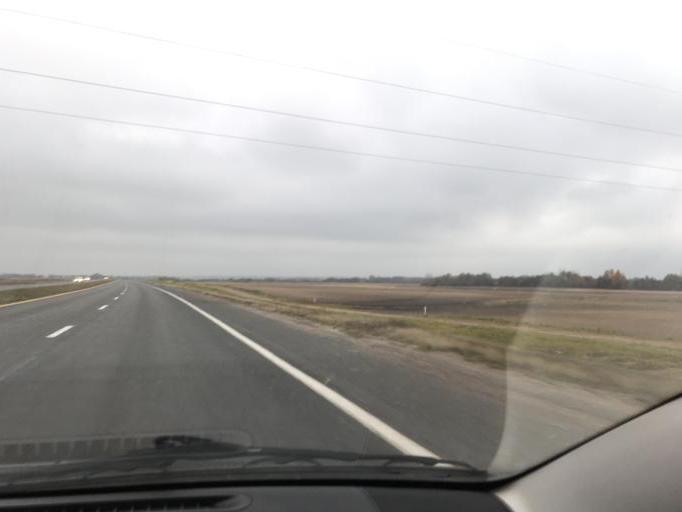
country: BY
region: Vitebsk
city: Vitebsk
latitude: 55.1553
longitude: 30.0897
